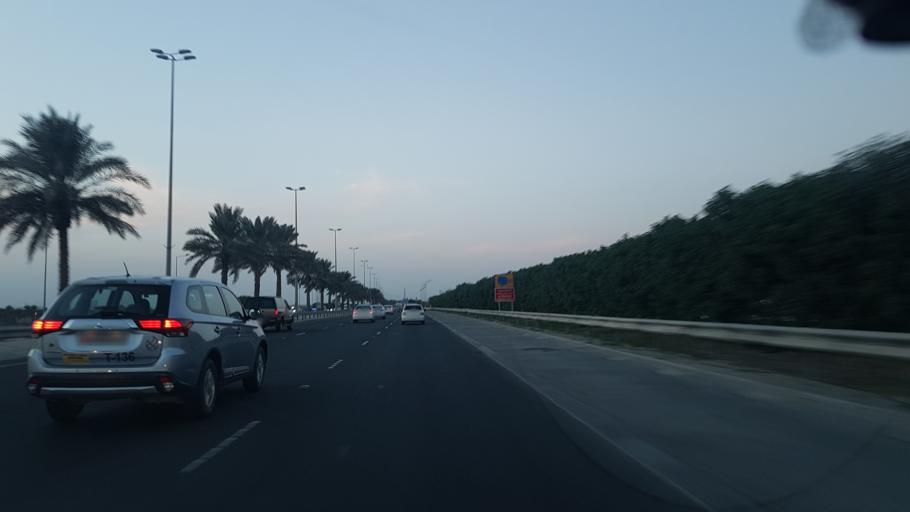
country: BH
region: Central Governorate
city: Madinat Hamad
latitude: 26.1504
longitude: 50.5086
